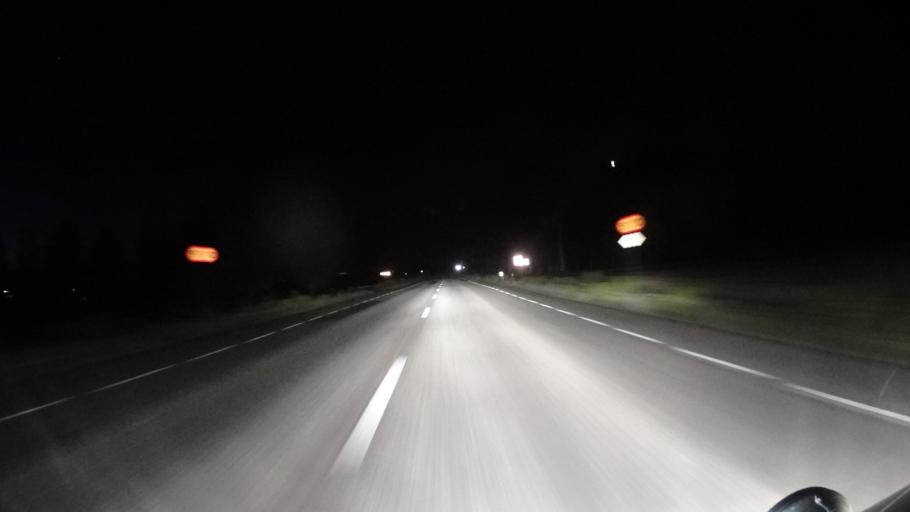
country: SE
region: OEstergoetland
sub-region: Vadstena Kommun
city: Herrestad
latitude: 58.3045
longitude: 14.8381
